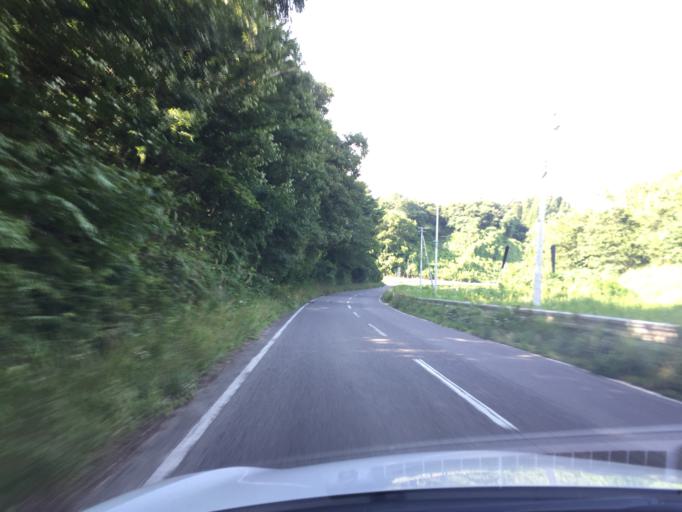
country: JP
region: Fukushima
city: Ishikawa
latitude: 37.2097
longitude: 140.4833
